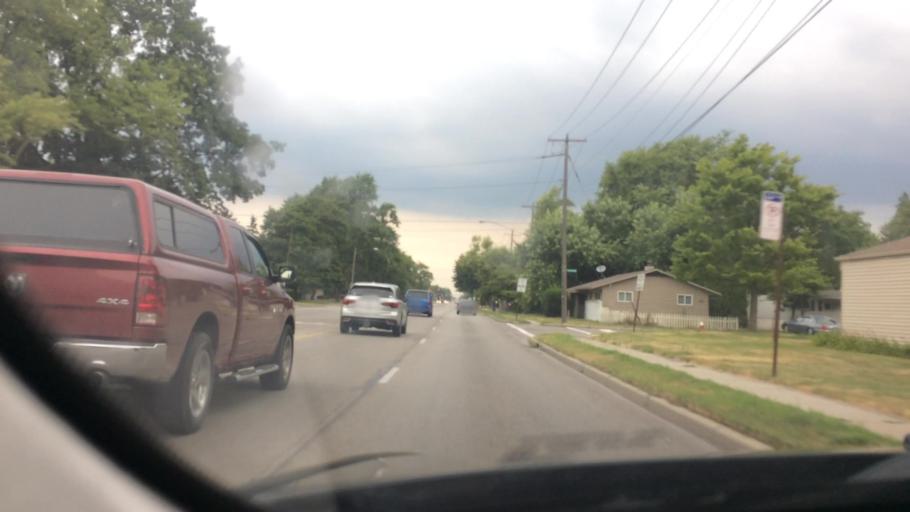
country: US
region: Ohio
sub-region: Wood County
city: Perrysburg
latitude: 41.6052
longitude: -83.6256
